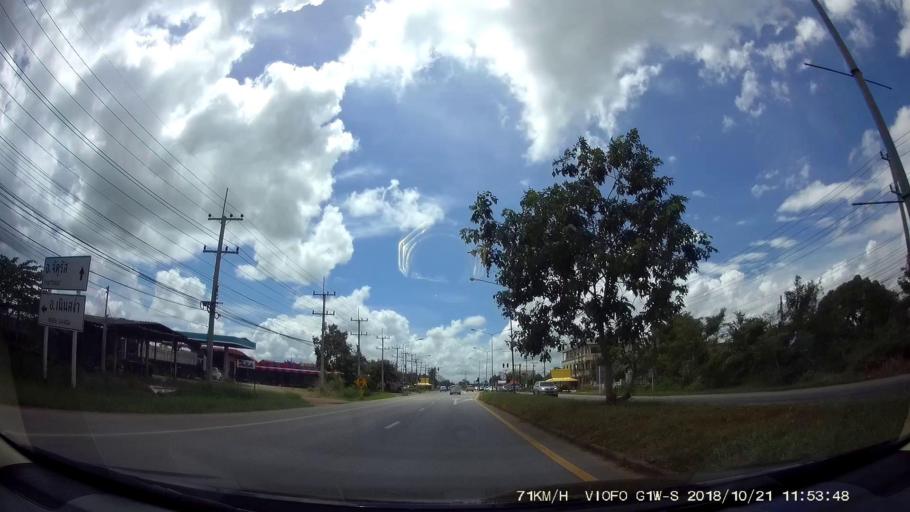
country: TH
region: Chaiyaphum
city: Chatturat
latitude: 15.5916
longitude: 101.9043
